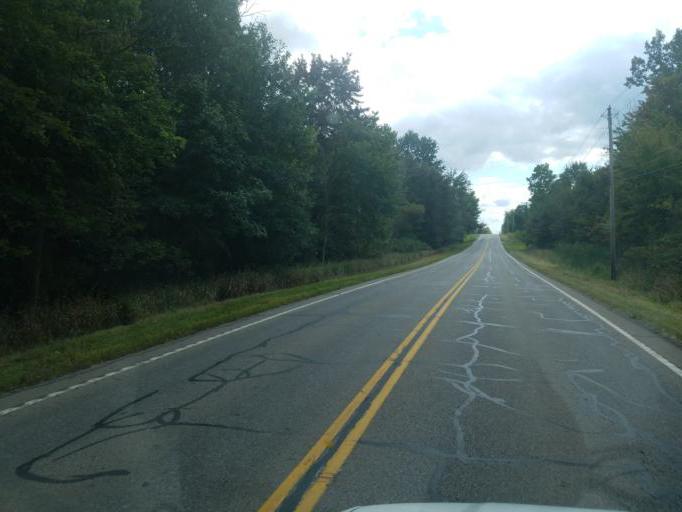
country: US
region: Ohio
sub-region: Richland County
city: Lincoln Heights
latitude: 40.8756
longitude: -82.5134
